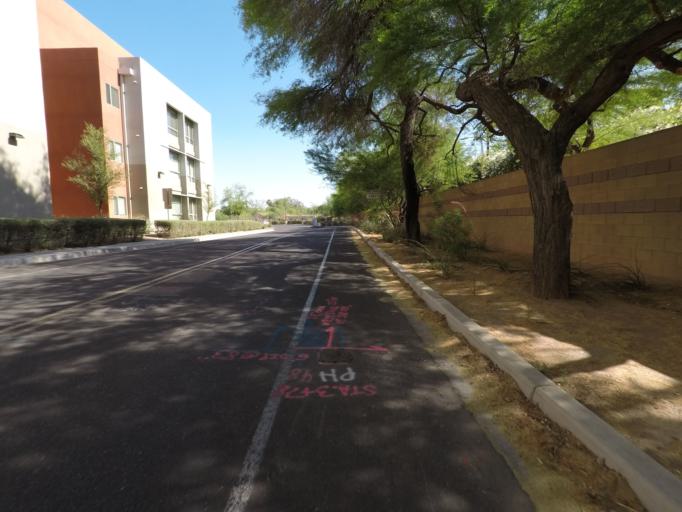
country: US
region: Arizona
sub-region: Maricopa County
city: Tempe Junction
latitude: 33.4119
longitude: -111.9306
